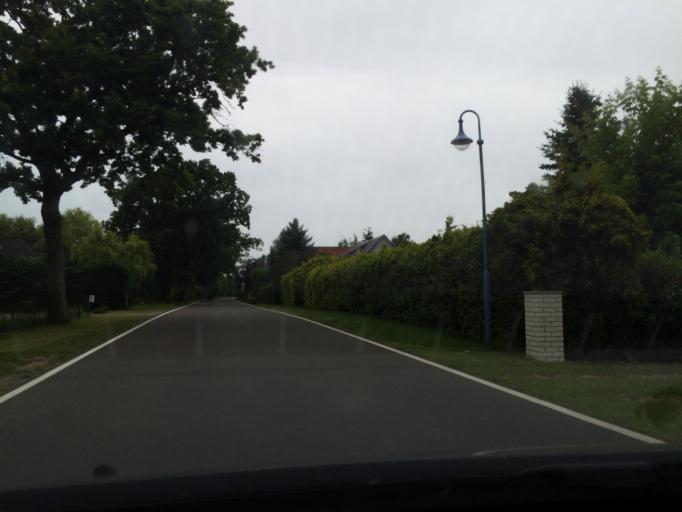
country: DE
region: Mecklenburg-Vorpommern
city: Prohn
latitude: 54.4144
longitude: 13.0145
